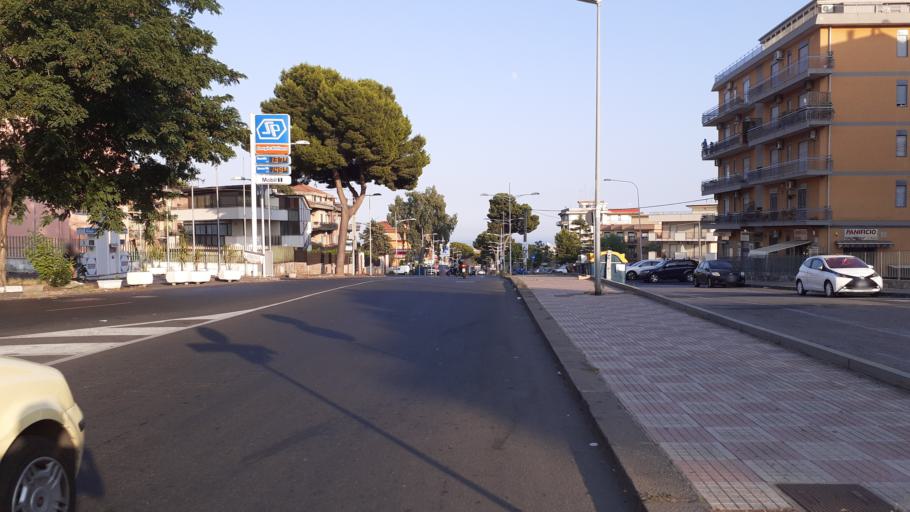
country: IT
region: Sicily
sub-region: Catania
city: Misterbianco
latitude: 37.5073
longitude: 15.0508
